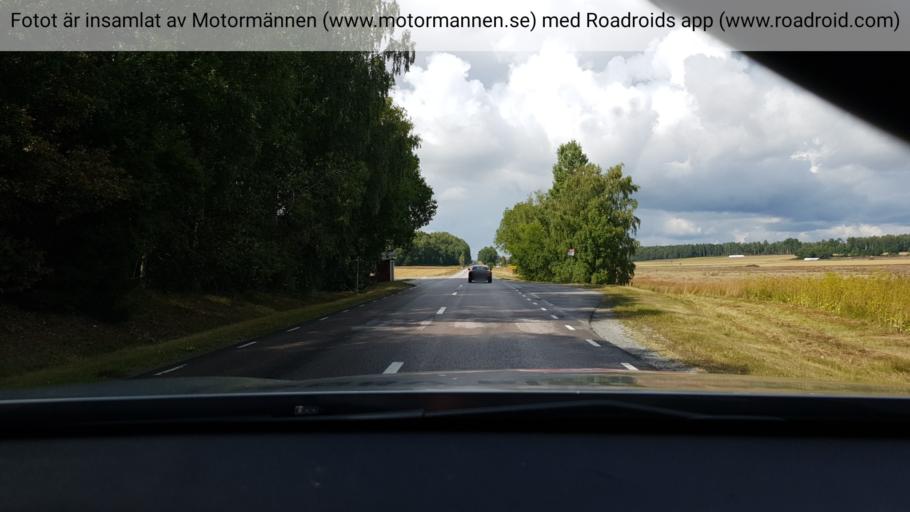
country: SE
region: Stockholm
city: Stenhamra
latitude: 59.3587
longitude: 17.6216
